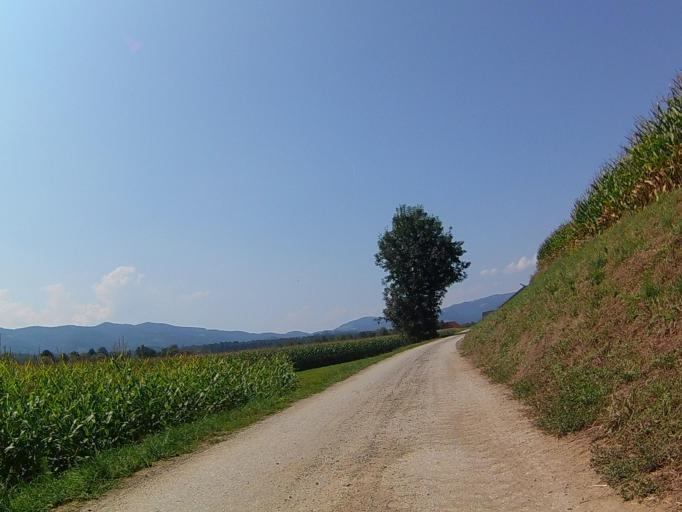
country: AT
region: Styria
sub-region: Politischer Bezirk Deutschlandsberg
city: Pitschgau
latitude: 46.7037
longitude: 15.2918
